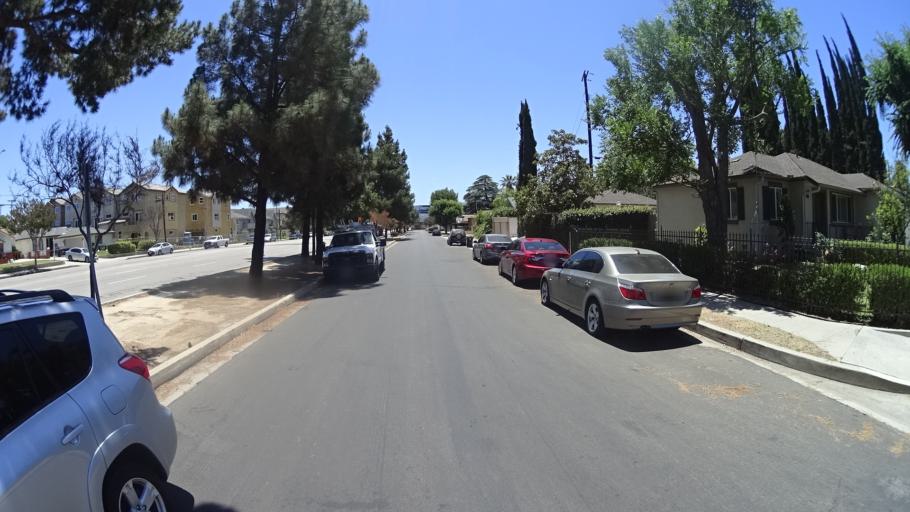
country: US
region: California
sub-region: Los Angeles County
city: Northridge
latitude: 34.1971
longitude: -118.5014
